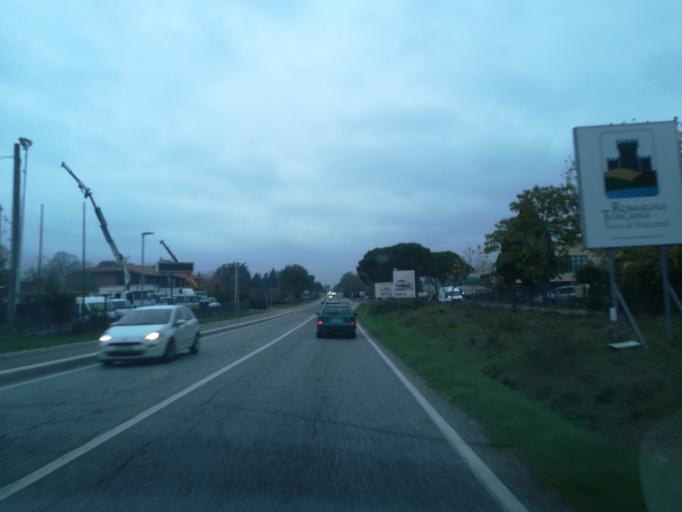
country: IT
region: Emilia-Romagna
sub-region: Provincia di Bologna
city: Toscanella
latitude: 44.3785
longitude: 11.6497
